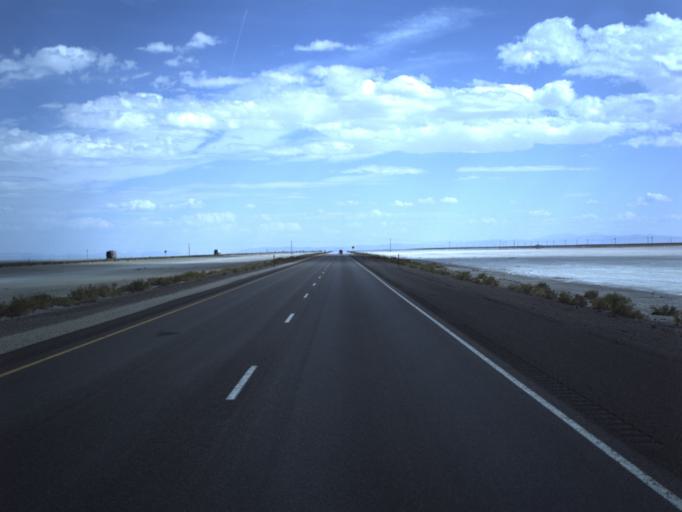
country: US
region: Utah
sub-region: Tooele County
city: Wendover
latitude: 40.7370
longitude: -113.7768
